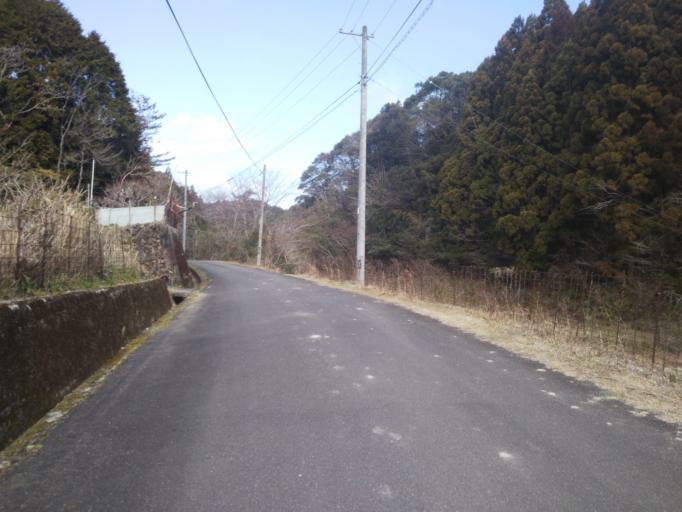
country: JP
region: Kochi
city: Nakamura
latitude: 33.0353
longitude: 132.9852
